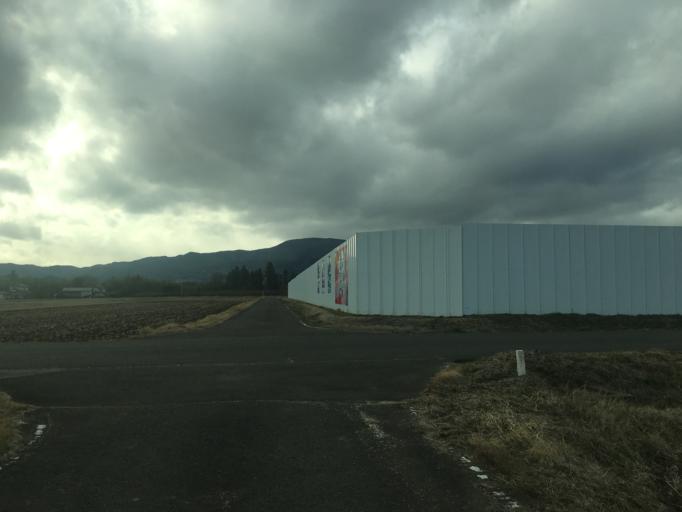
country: JP
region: Fukushima
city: Yanagawamachi-saiwaicho
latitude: 37.8814
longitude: 140.5822
